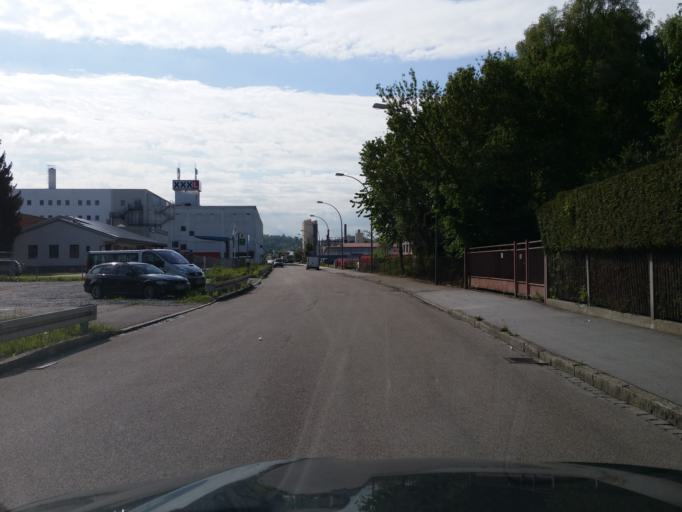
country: DE
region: Bavaria
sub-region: Lower Bavaria
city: Landshut
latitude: 48.5560
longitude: 12.1456
